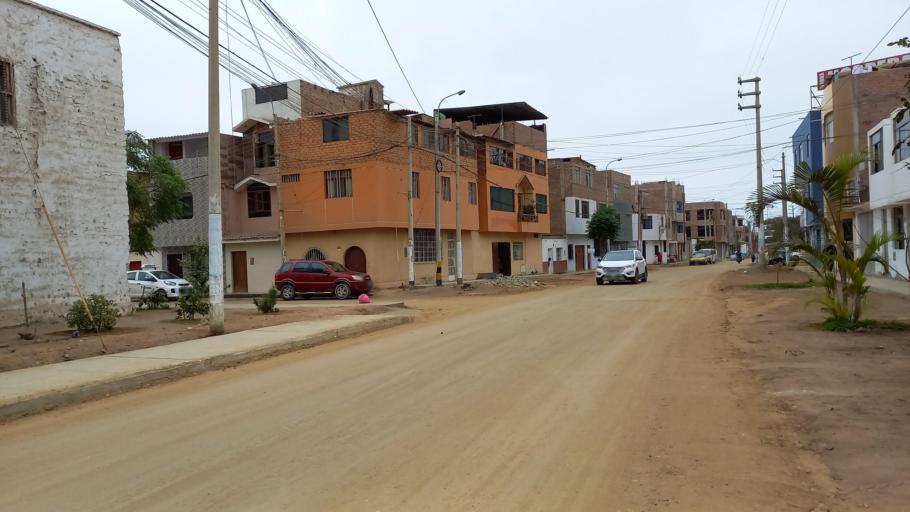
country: PE
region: La Libertad
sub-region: Provincia de Trujillo
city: Trujillo
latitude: -8.1027
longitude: -79.0436
